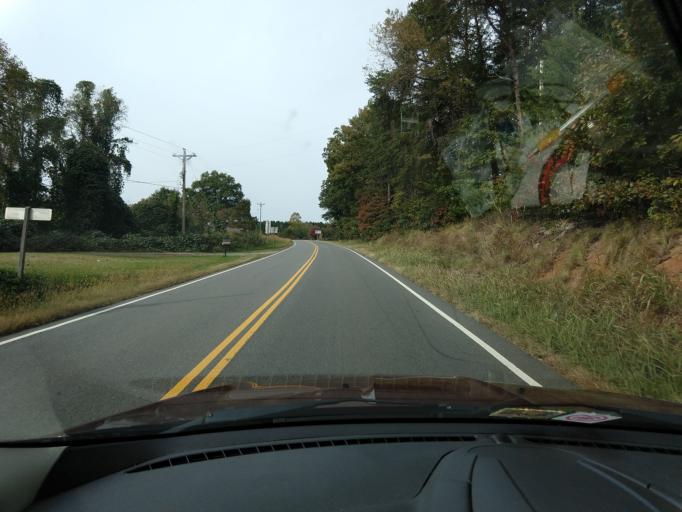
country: US
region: Virginia
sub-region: Franklin County
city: Union Hall
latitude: 36.9561
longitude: -79.5362
